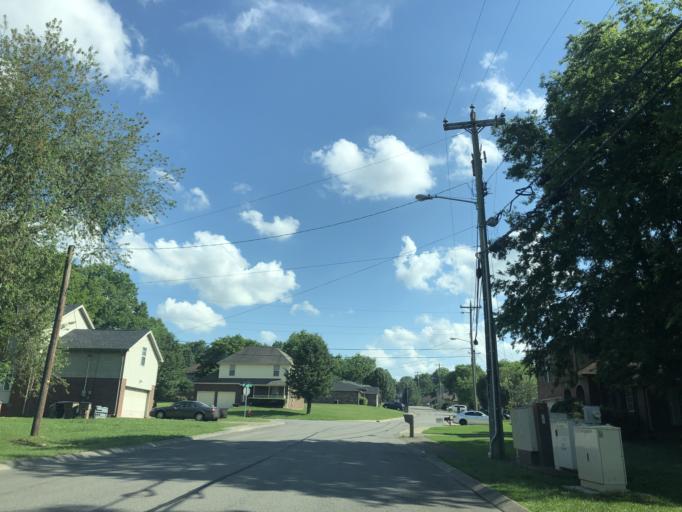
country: US
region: Tennessee
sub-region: Davidson County
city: Nashville
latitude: 36.2312
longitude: -86.8018
